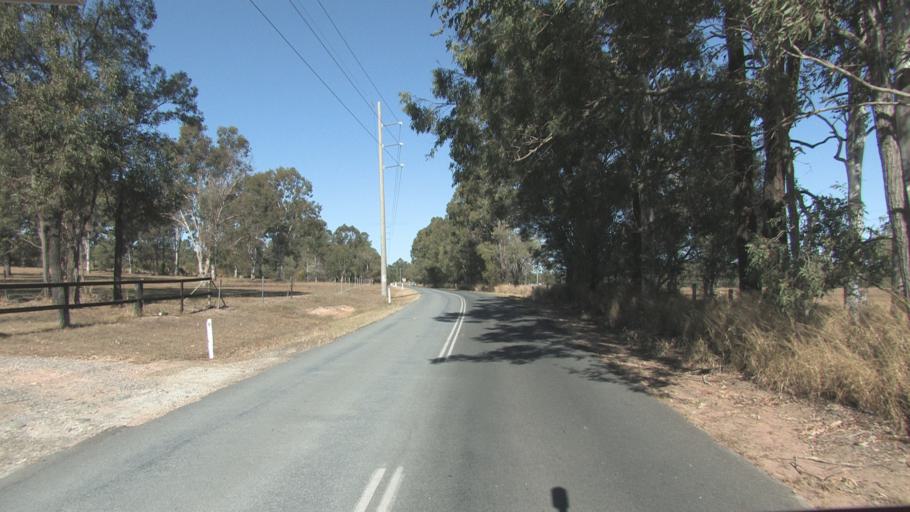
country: AU
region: Queensland
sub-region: Logan
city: Cedar Vale
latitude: -27.8640
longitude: 153.0177
